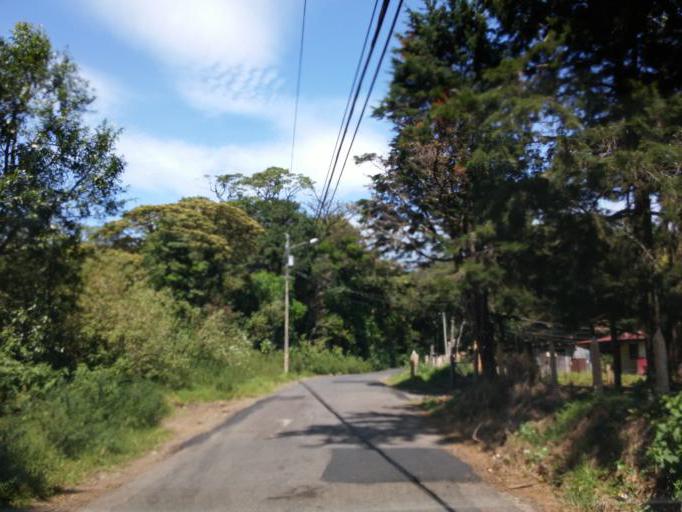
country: CR
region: Heredia
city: Santo Domingo
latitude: 10.0907
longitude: -84.1081
